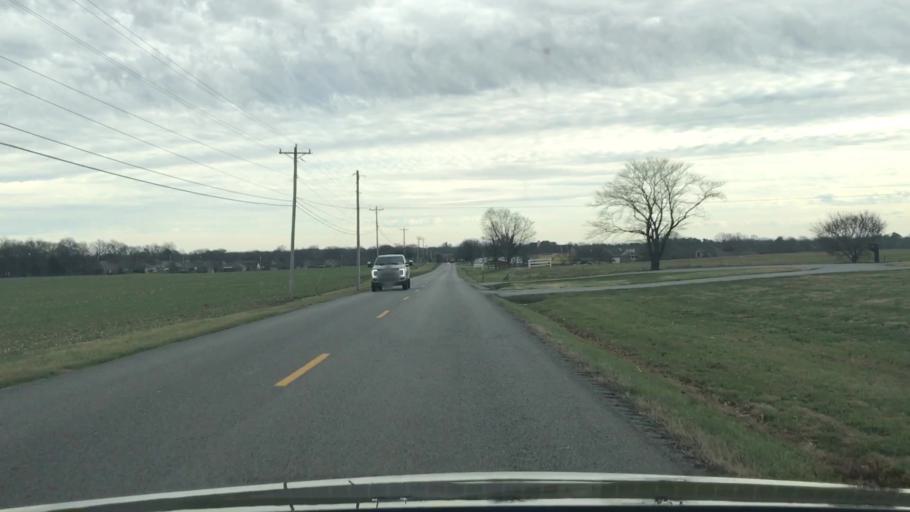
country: US
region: Kentucky
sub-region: Christian County
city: Hopkinsville
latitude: 36.8607
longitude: -87.5320
